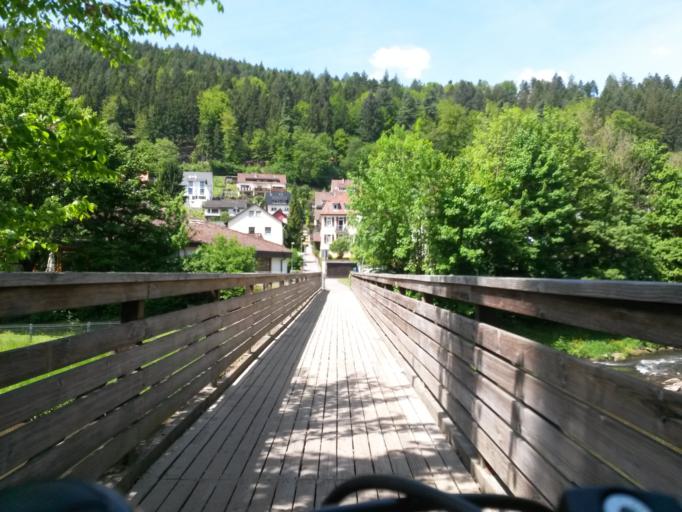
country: DE
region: Baden-Wuerttemberg
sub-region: Karlsruhe Region
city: Calw
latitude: 48.7336
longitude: 8.7337
